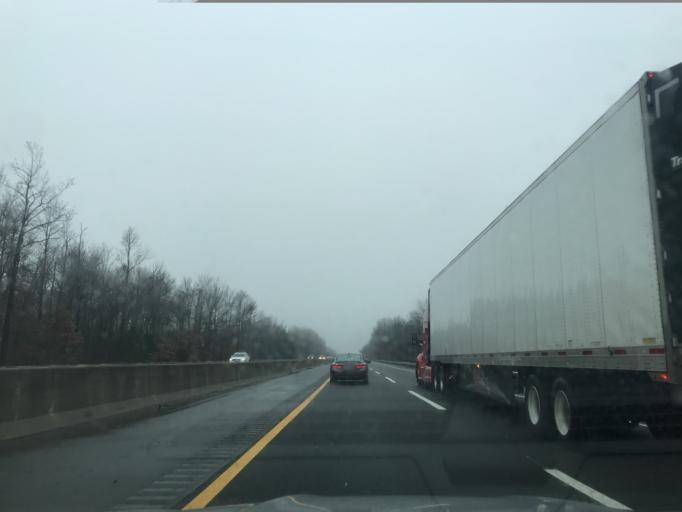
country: US
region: New Jersey
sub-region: Gloucester County
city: Mullica Hill
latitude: 39.7674
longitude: -75.2536
